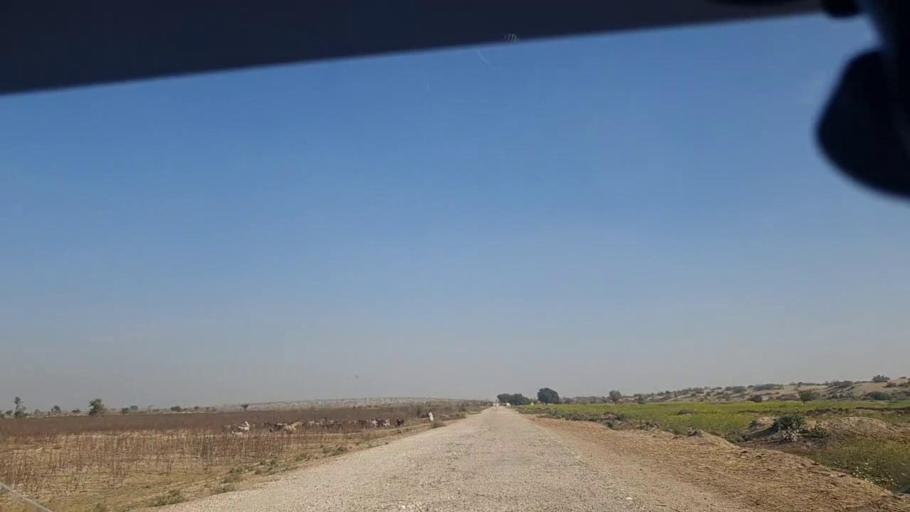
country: PK
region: Sindh
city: Khanpur
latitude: 27.5583
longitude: 69.3295
